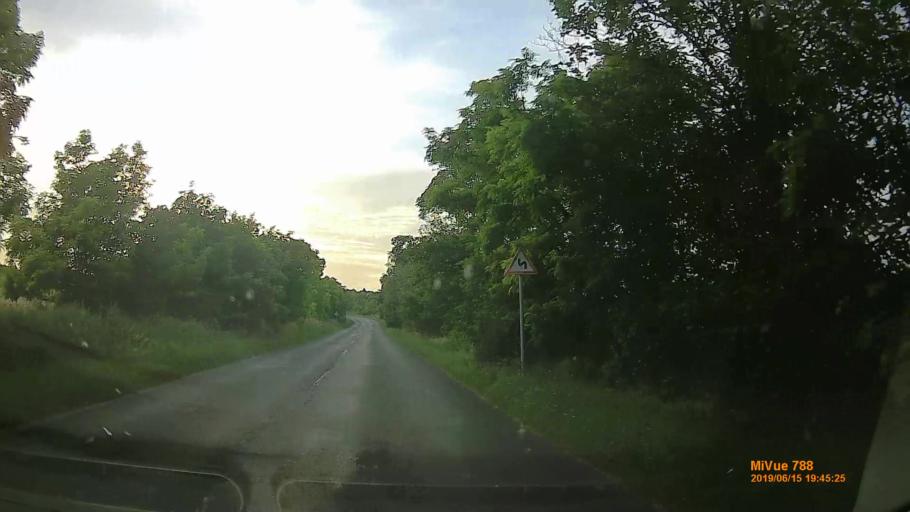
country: HU
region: Veszprem
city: Szentkiralyszabadja
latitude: 47.0094
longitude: 17.9648
